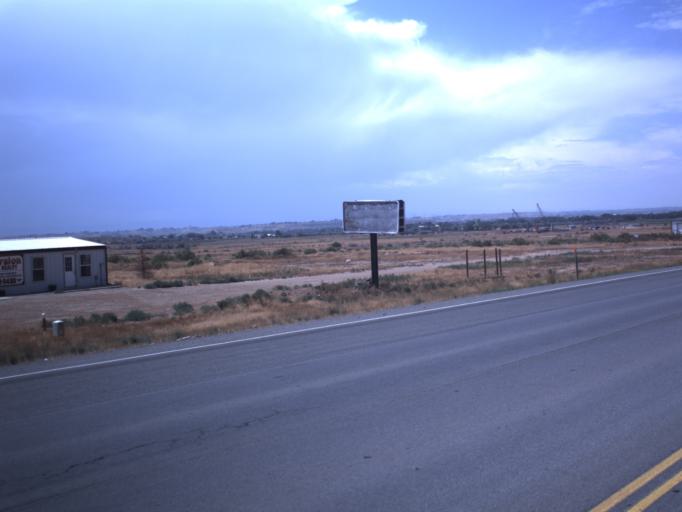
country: US
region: Utah
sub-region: Duchesne County
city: Roosevelt
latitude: 40.3023
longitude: -109.9359
